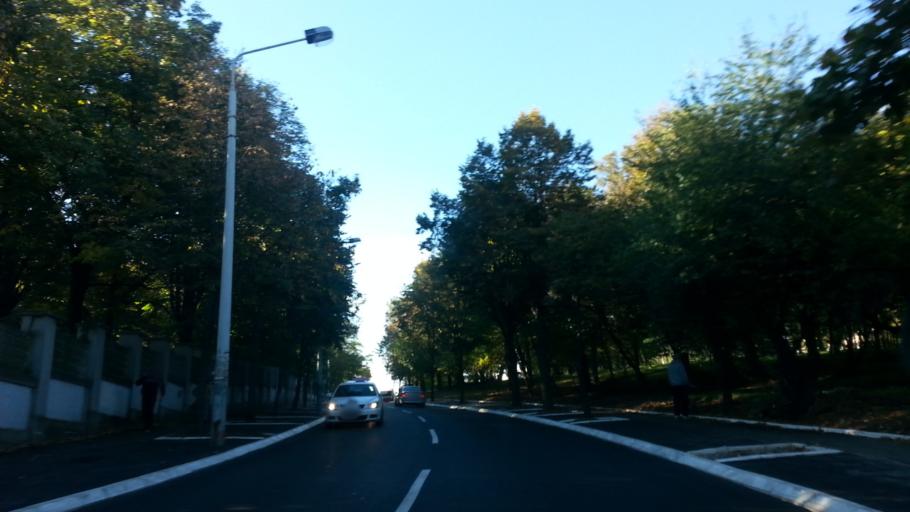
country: RS
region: Central Serbia
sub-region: Belgrade
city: Savski Venac
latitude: 44.7809
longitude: 20.4592
